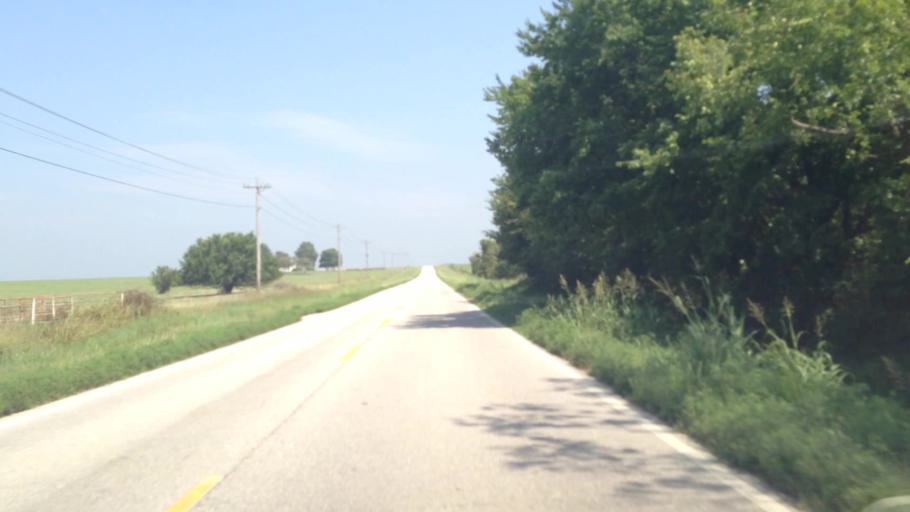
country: US
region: Oklahoma
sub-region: Craig County
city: Vinita
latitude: 36.7336
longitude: -95.1436
